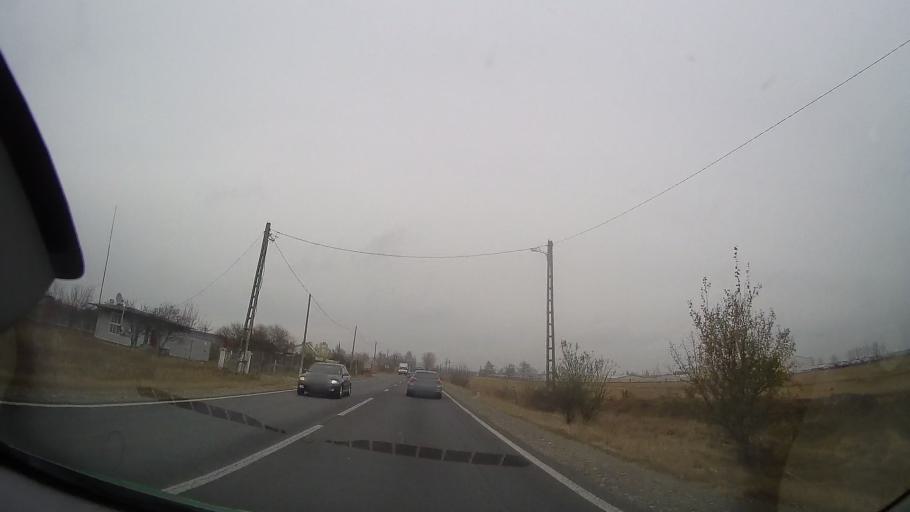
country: RO
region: Prahova
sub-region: Comuna Blejoiu
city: Ploiestiori
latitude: 44.9802
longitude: 25.9966
